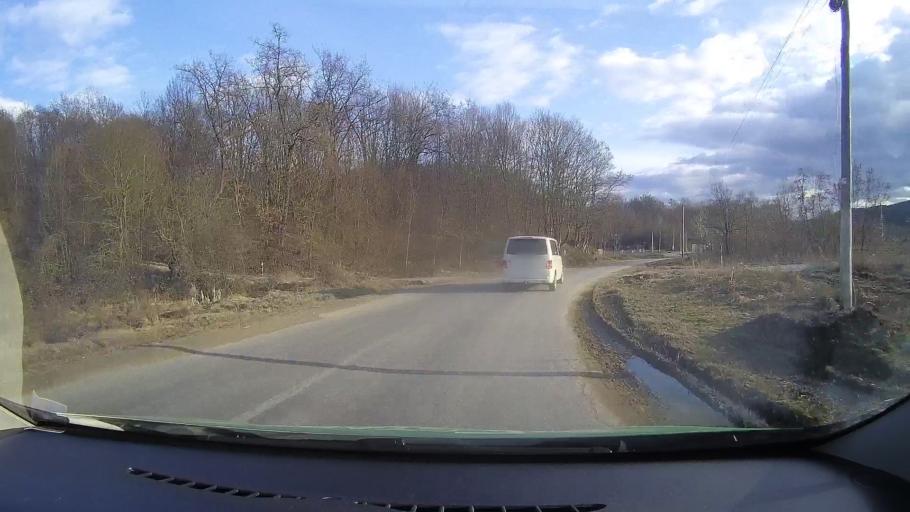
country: RO
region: Dambovita
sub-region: Comuna Ocnita
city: Ocnita
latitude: 44.9688
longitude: 25.5481
